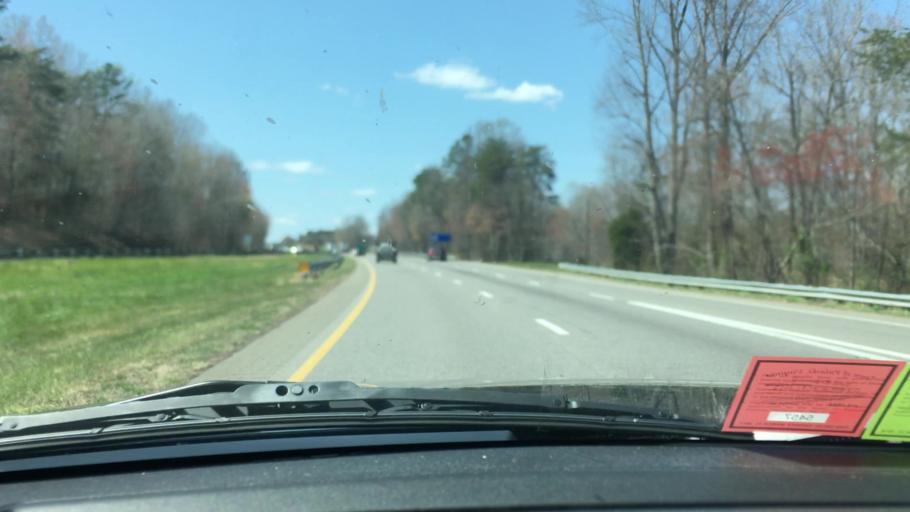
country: US
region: North Carolina
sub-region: Surry County
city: Pilot Mountain
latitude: 36.4028
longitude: -80.4932
